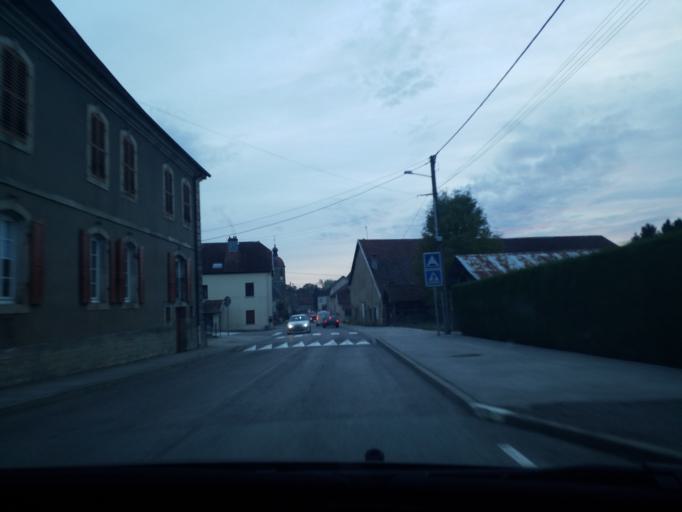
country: FR
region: Franche-Comte
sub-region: Departement de la Haute-Saone
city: Magny-Vernois
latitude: 47.6474
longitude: 6.4477
